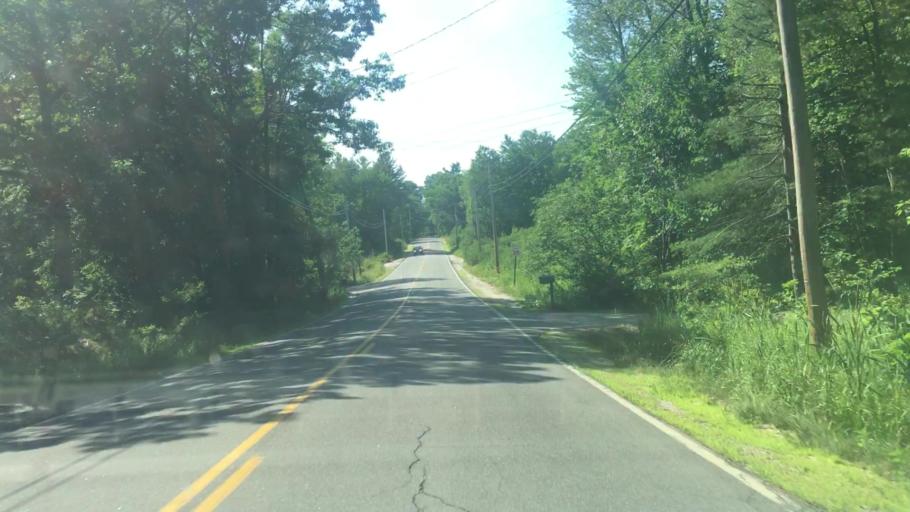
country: US
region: Maine
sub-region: York County
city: Hollis Center
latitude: 43.6455
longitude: -70.5861
